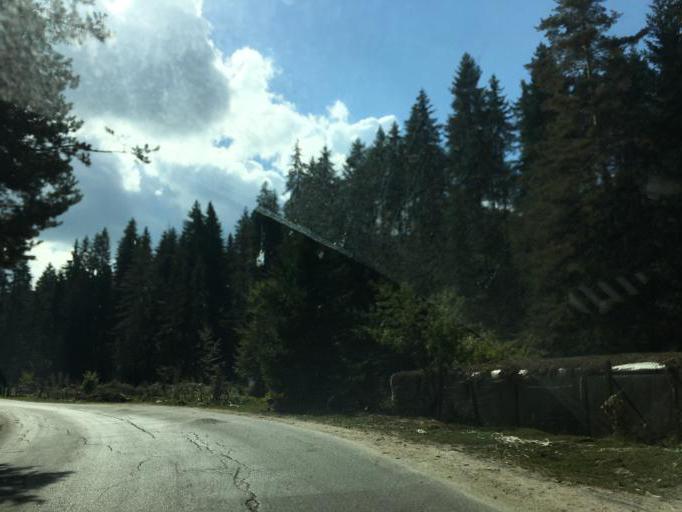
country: BG
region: Pazardzhik
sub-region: Obshtina Batak
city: Batak
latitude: 41.9275
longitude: 24.2749
